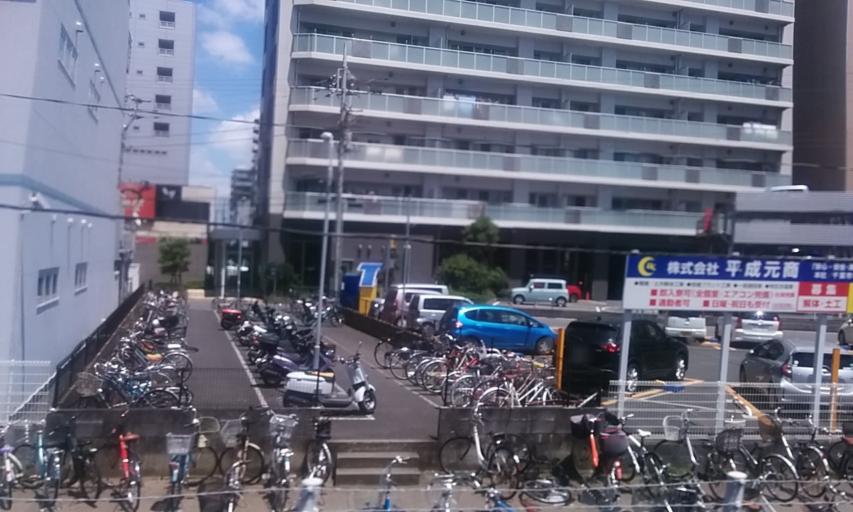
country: JP
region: Chiba
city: Chiba
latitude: 35.5805
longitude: 140.1318
